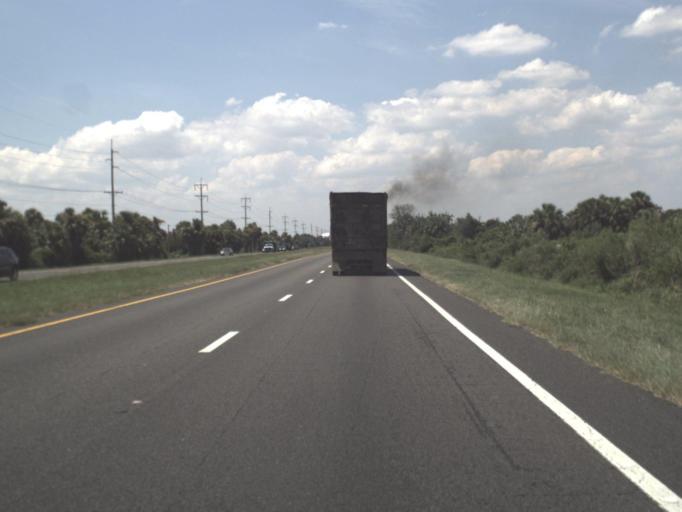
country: US
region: Florida
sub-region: Hillsborough County
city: Gibsonton
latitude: 27.8785
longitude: -82.3929
